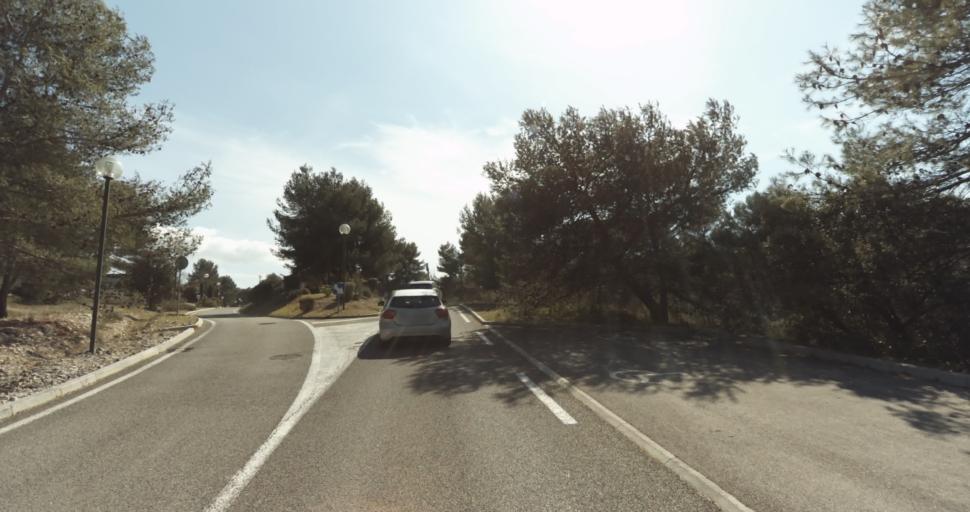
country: FR
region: Provence-Alpes-Cote d'Azur
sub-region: Departement des Bouches-du-Rhone
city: Cabries
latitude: 43.4762
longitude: 5.3677
